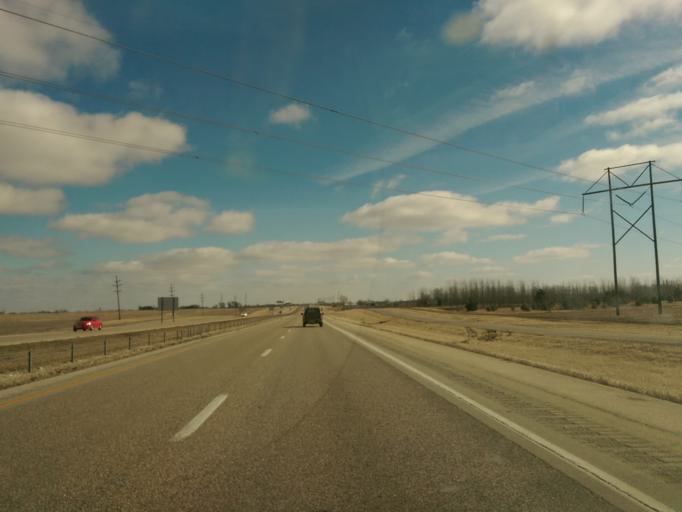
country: US
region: Missouri
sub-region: Montgomery County
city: Montgomery City
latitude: 38.8931
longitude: -91.4337
